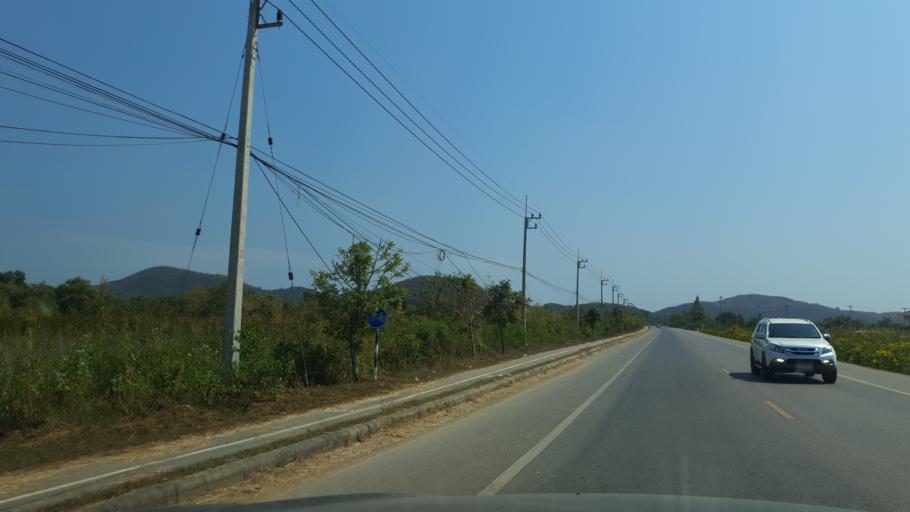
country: TH
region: Prachuap Khiri Khan
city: Pran Buri
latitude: 12.3391
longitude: 99.9481
